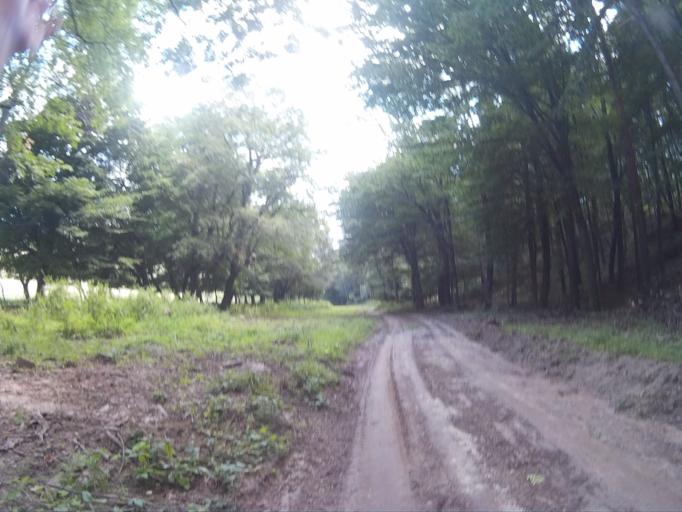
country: HU
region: Veszprem
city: Zirc
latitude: 47.1986
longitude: 17.9161
